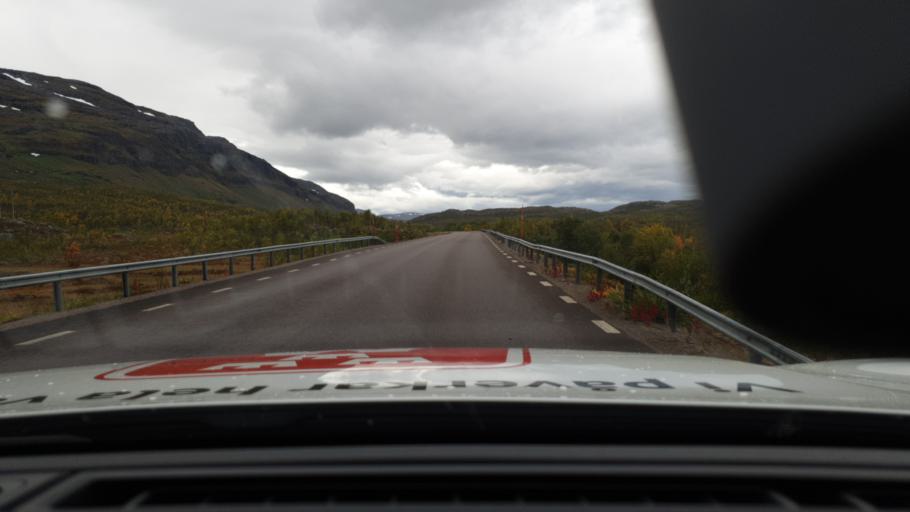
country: NO
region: Troms
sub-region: Bardu
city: Setermoen
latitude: 68.4306
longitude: 18.5008
